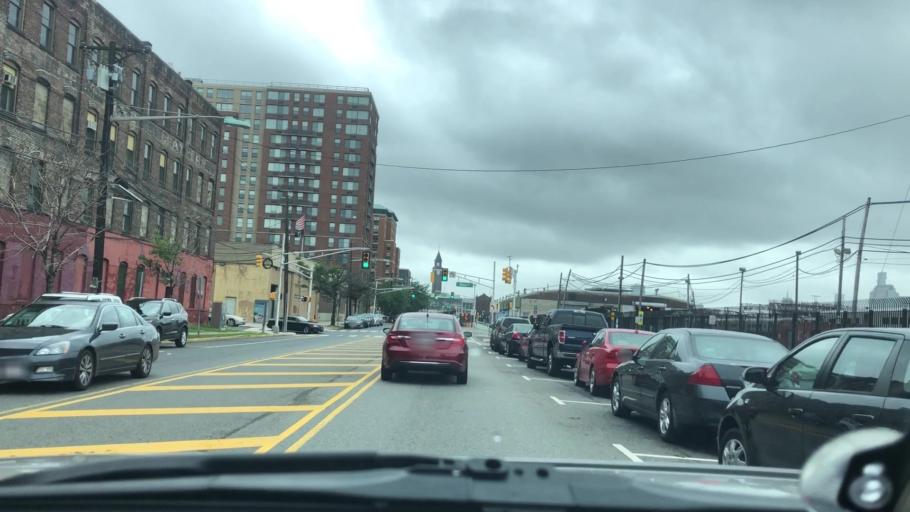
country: US
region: New Jersey
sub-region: Hudson County
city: Hoboken
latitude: 40.7363
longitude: -74.0357
